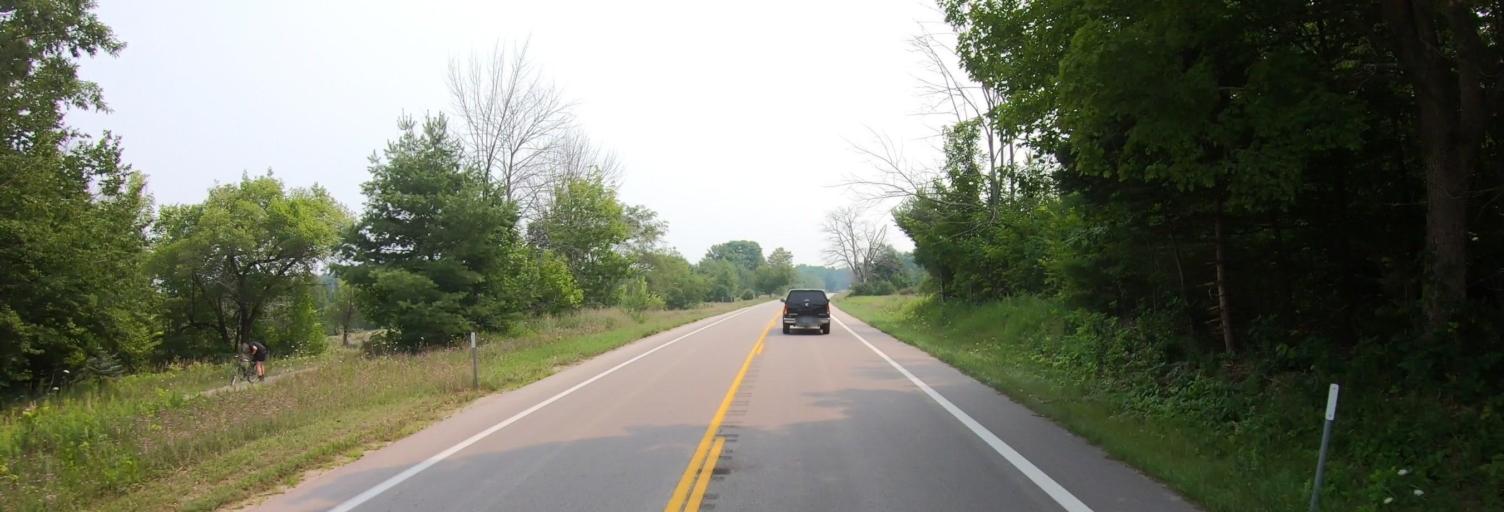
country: US
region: Michigan
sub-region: Leelanau County
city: Leland
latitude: 44.9334
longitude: -85.9032
